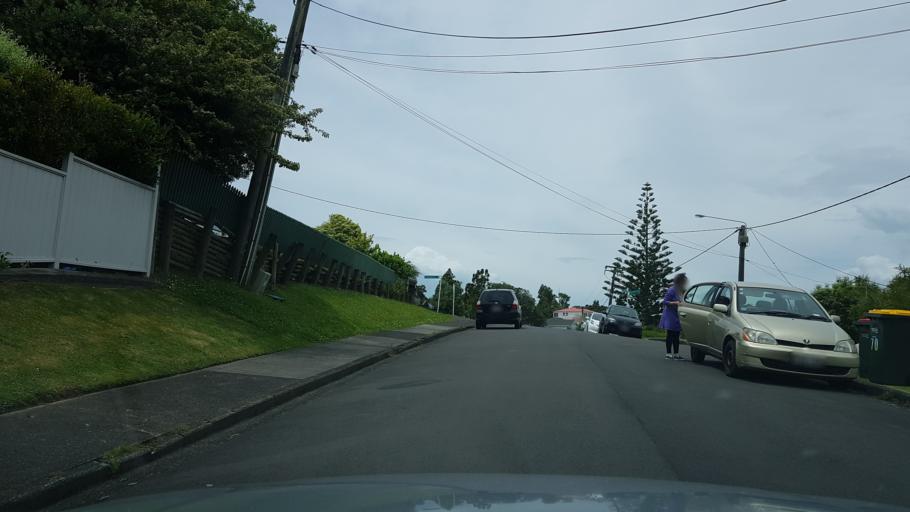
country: NZ
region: Auckland
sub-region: Auckland
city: North Shore
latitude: -36.8155
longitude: 174.7279
